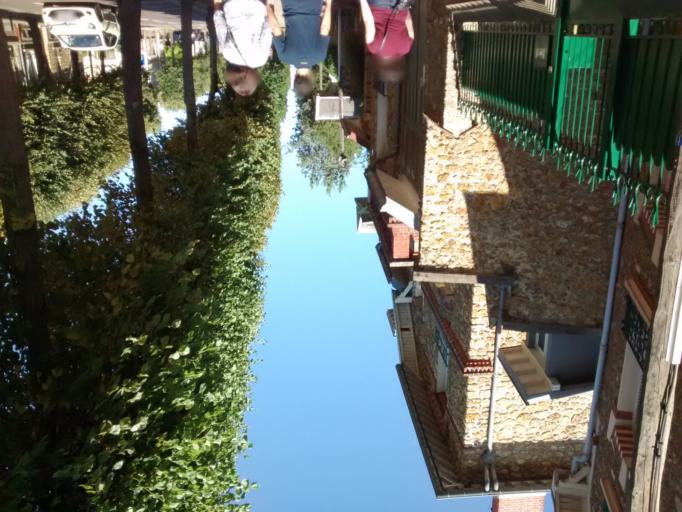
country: FR
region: Ile-de-France
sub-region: Departement des Yvelines
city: Viroflay
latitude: 48.8058
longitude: 2.1507
